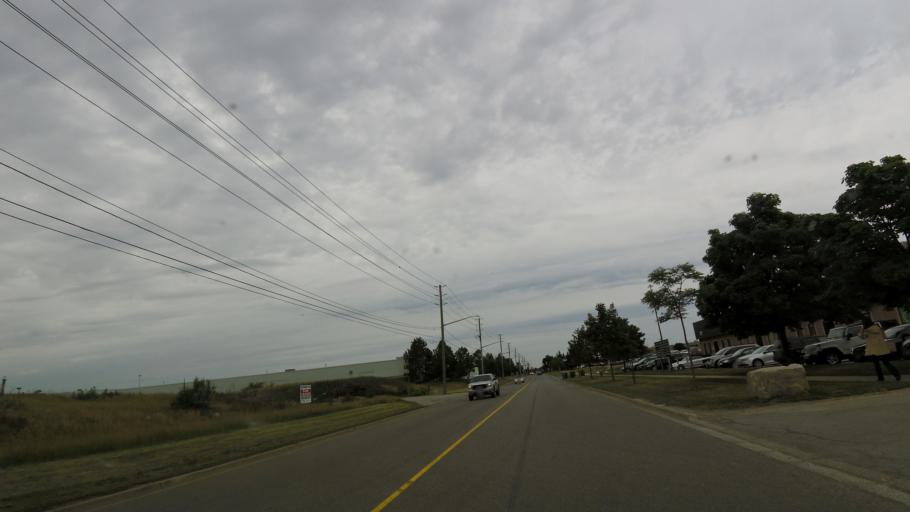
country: CA
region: Ontario
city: Oakville
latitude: 43.4167
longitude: -79.7272
